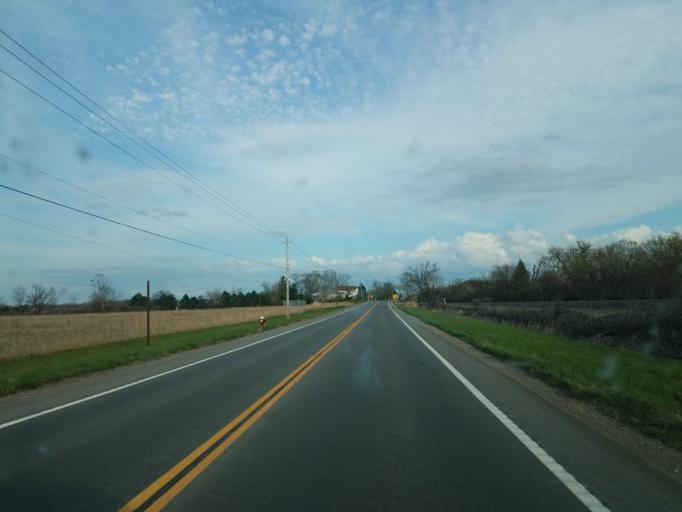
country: US
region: Ohio
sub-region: Erie County
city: Huron
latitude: 41.4152
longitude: -82.6222
